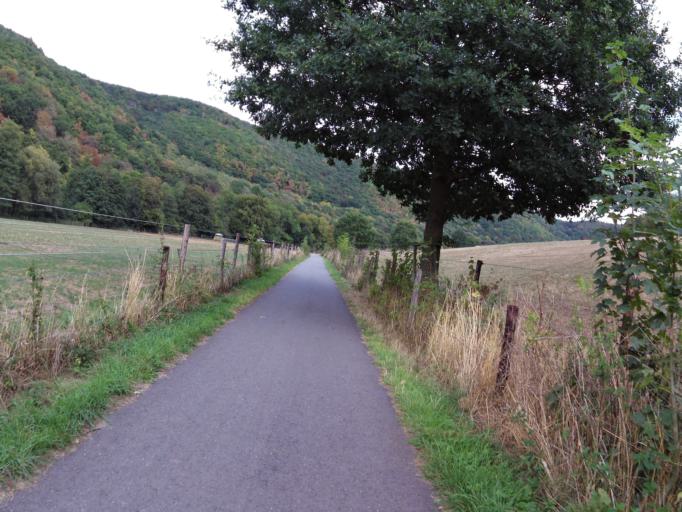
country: DE
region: North Rhine-Westphalia
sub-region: Regierungsbezirk Koln
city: Nideggen
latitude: 50.7004
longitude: 6.4549
